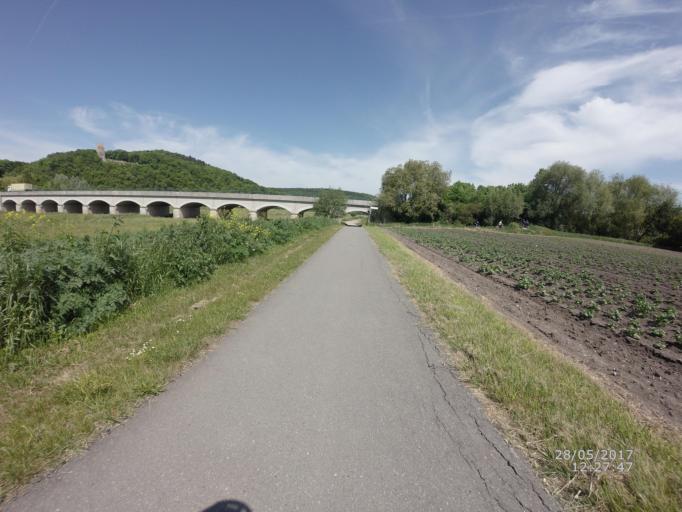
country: DE
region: Thuringia
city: Oldisleben
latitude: 51.2908
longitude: 11.1694
